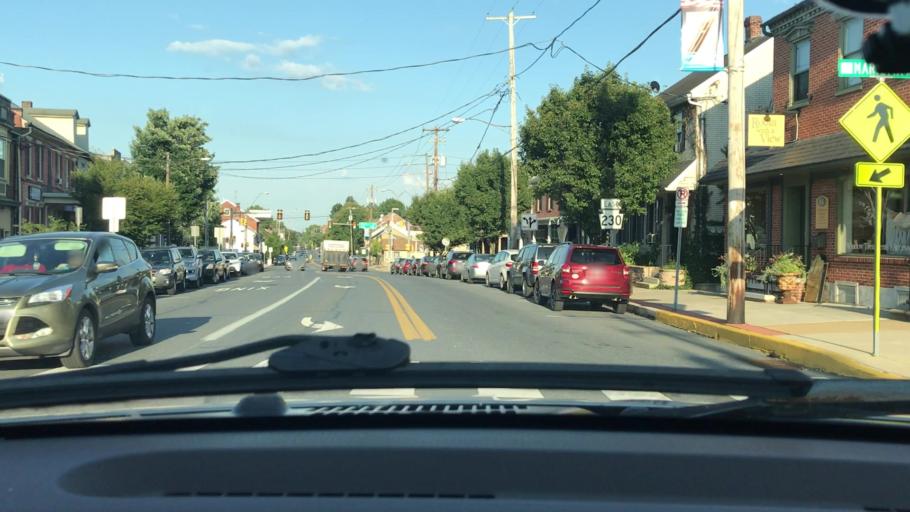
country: US
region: Pennsylvania
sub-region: Lancaster County
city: Mount Joy
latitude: 40.1093
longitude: -76.5001
